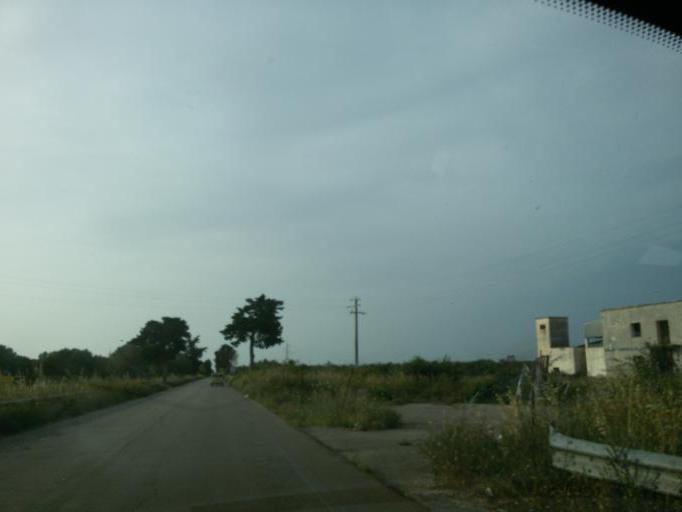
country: IT
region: Apulia
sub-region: Provincia di Brindisi
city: Tuturano
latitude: 40.5324
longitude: 17.9821
